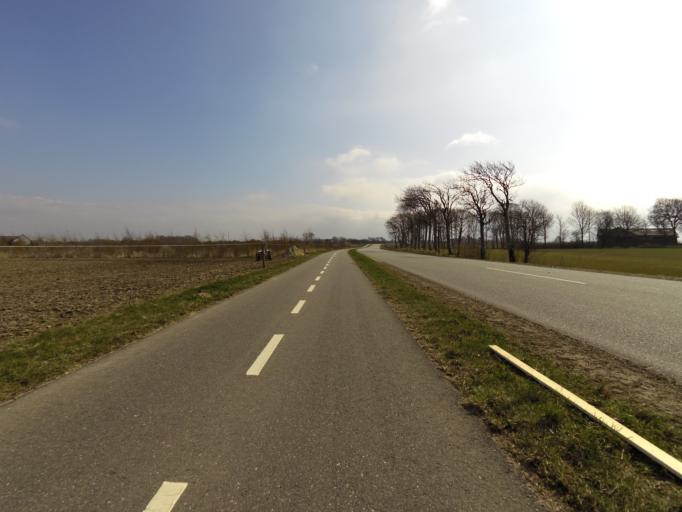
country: DK
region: Central Jutland
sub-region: Struer Kommune
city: Struer
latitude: 56.4473
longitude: 8.6235
